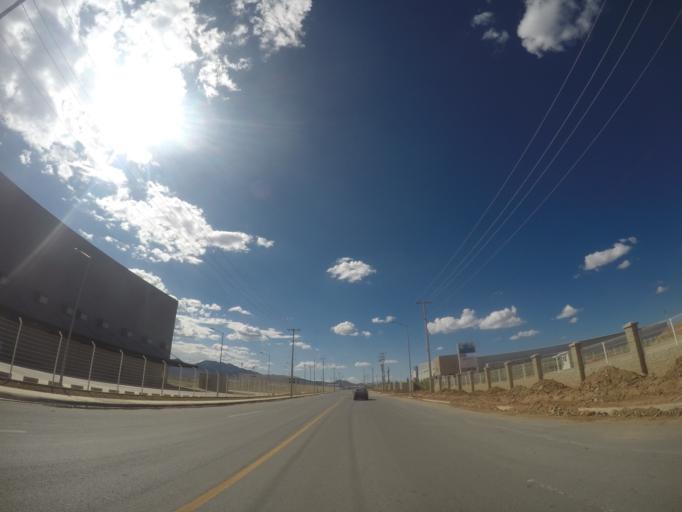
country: MX
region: San Luis Potosi
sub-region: Zaragoza
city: Cerro Gordo
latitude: 21.9760
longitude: -100.8547
